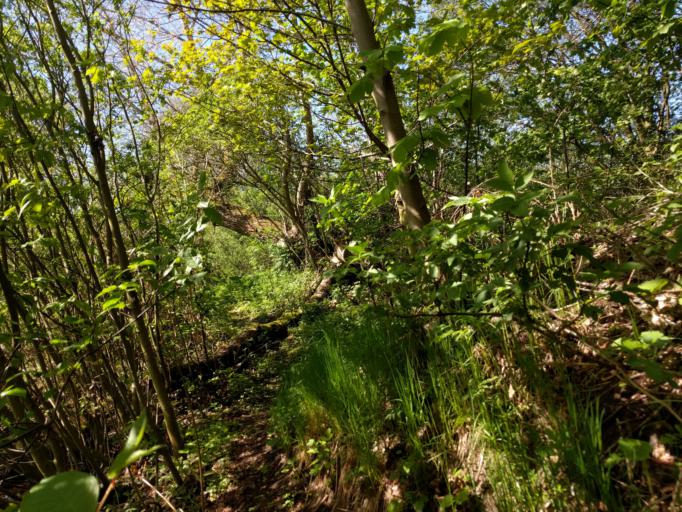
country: DK
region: South Denmark
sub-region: Kerteminde Kommune
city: Langeskov
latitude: 55.3886
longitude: 10.5596
